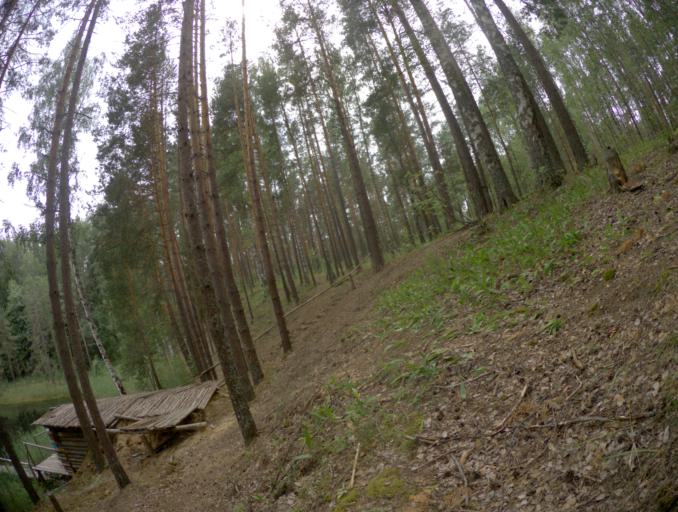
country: RU
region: Nizjnij Novgorod
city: Frolishchi
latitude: 56.3518
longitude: 42.7802
